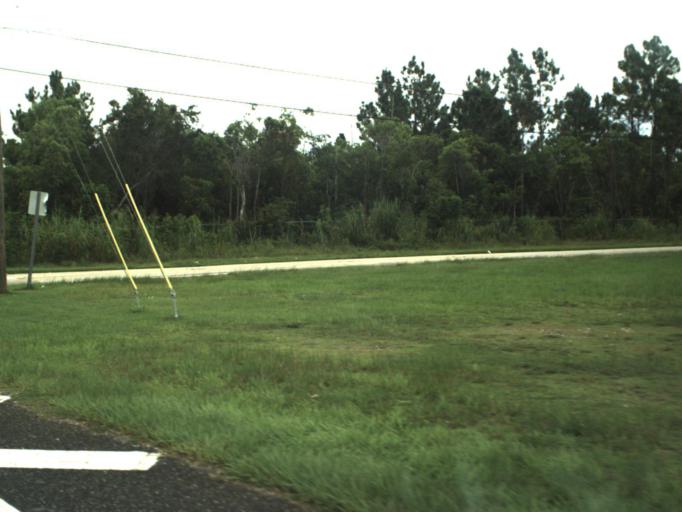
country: US
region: Florida
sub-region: Miami-Dade County
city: Florida City
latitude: 25.4402
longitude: -80.5015
